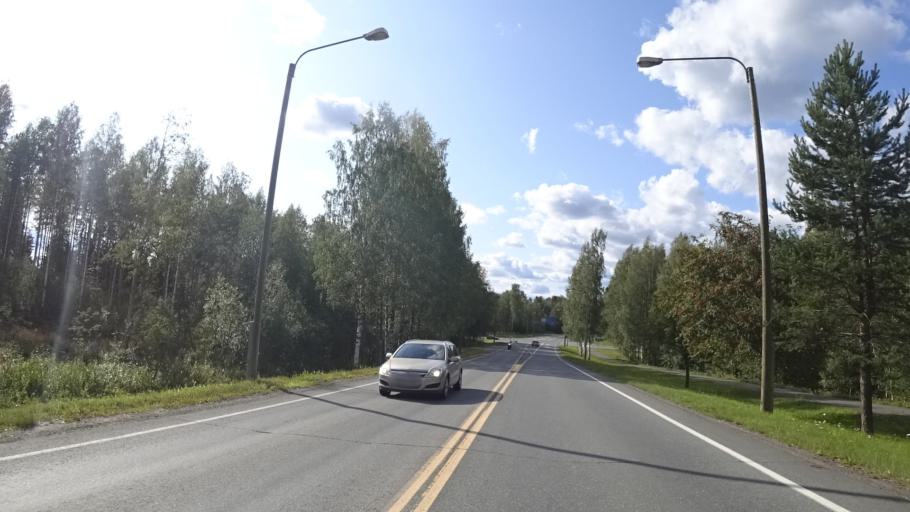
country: FI
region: North Karelia
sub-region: Keski-Karjala
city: Tohmajaervi
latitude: 62.2287
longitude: 30.3240
